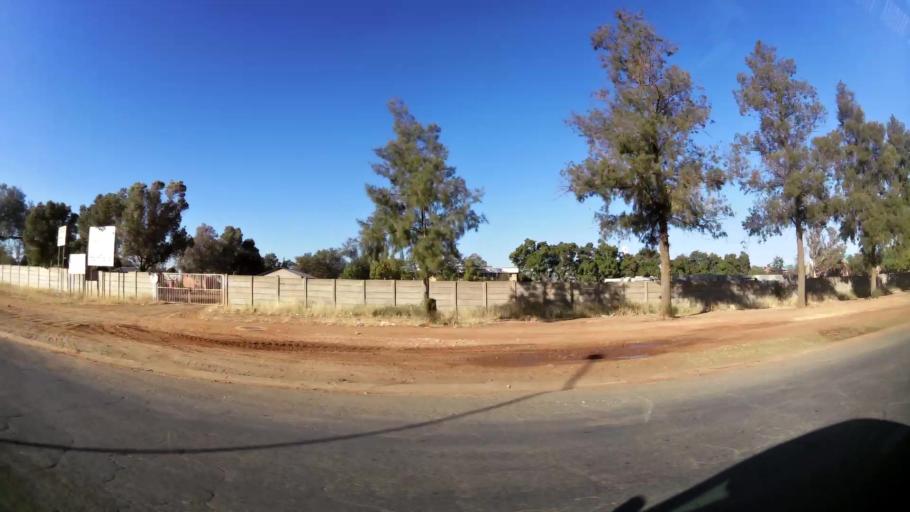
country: ZA
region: Northern Cape
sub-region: Frances Baard District Municipality
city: Kimberley
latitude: -28.7361
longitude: 24.7390
